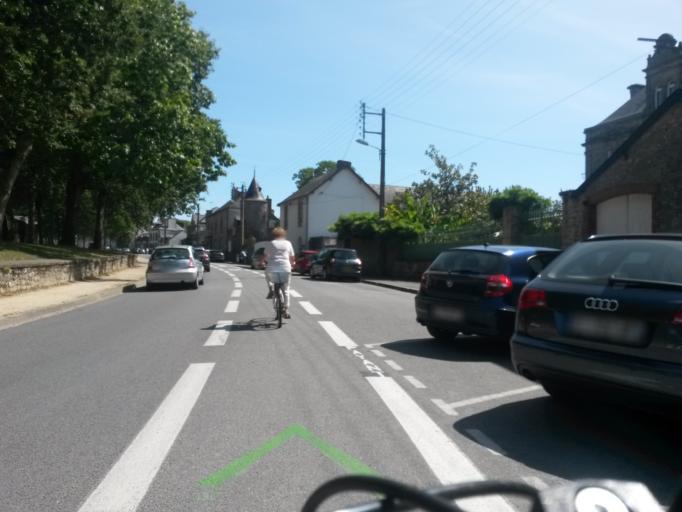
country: FR
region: Pays de la Loire
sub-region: Departement de la Loire-Atlantique
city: Guerande
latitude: 47.3266
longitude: -2.4325
